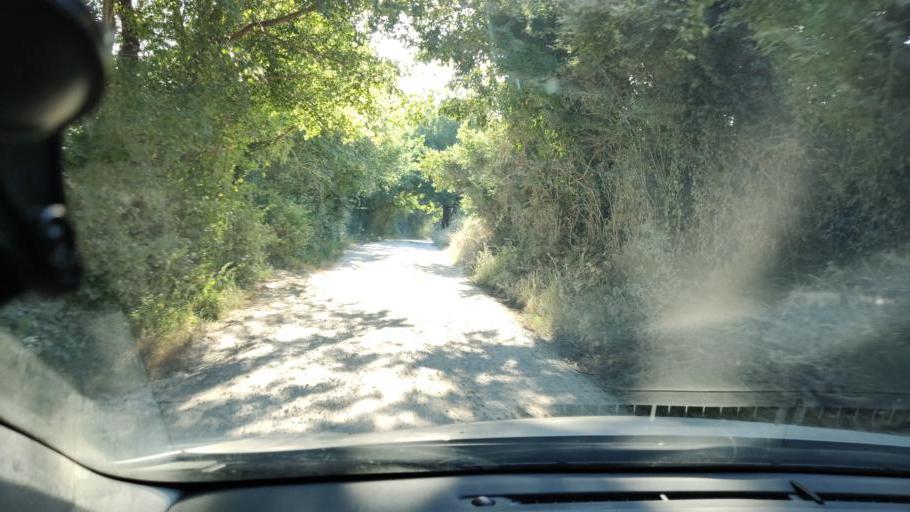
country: IT
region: Umbria
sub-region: Provincia di Terni
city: Amelia
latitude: 42.5454
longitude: 12.3924
